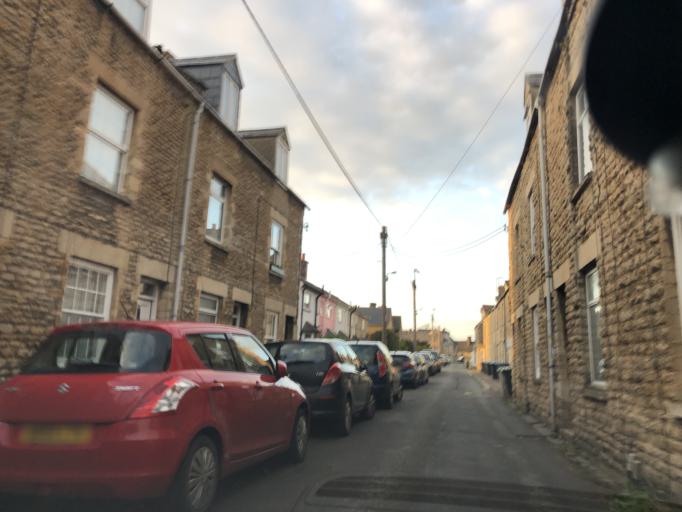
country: GB
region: England
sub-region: Oxfordshire
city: Witney
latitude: 51.7822
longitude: -1.4902
